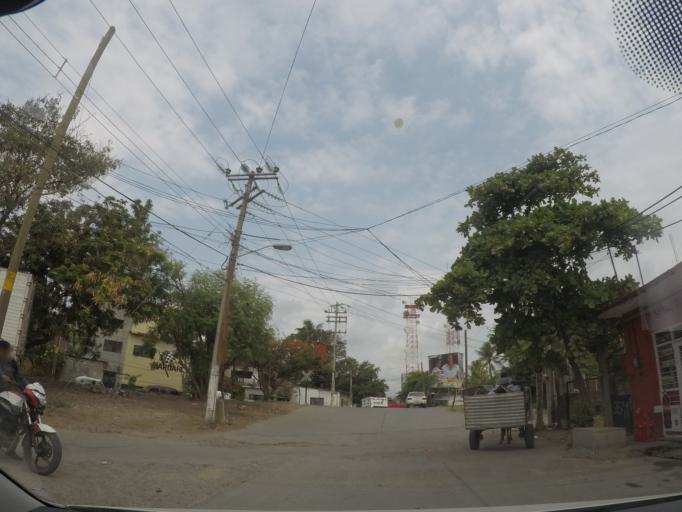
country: MX
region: Oaxaca
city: Juchitan de Zaragoza
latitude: 16.4419
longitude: -95.0195
